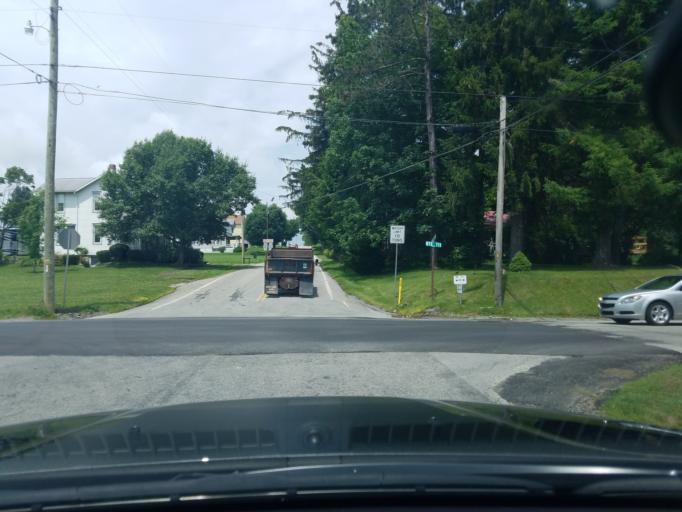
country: US
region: Pennsylvania
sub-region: Fayette County
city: Bear Rocks
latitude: 40.1501
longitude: -79.3330
